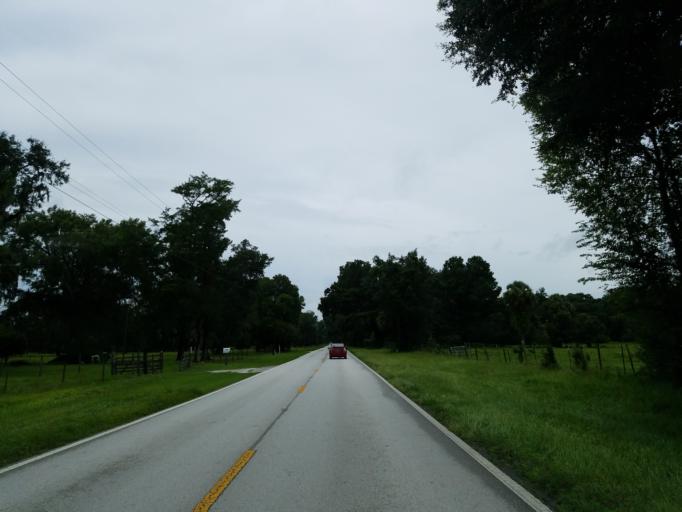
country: US
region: Florida
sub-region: Sumter County
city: Bushnell
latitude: 28.6910
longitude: -82.2019
